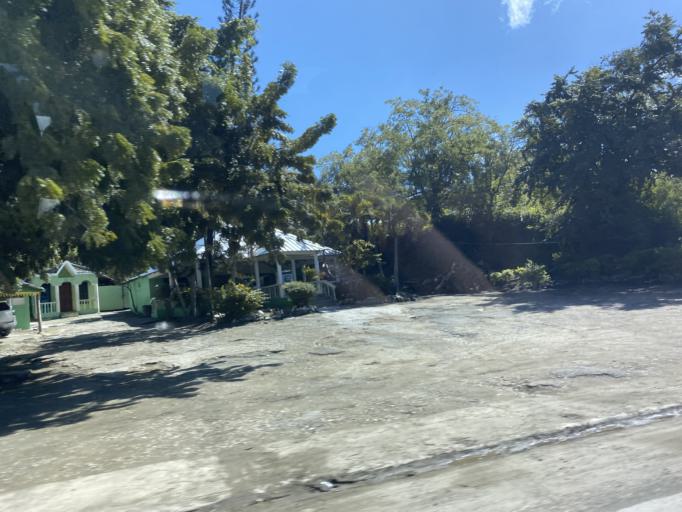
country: DO
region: Puerto Plata
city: Imbert
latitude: 19.8187
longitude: -70.7783
